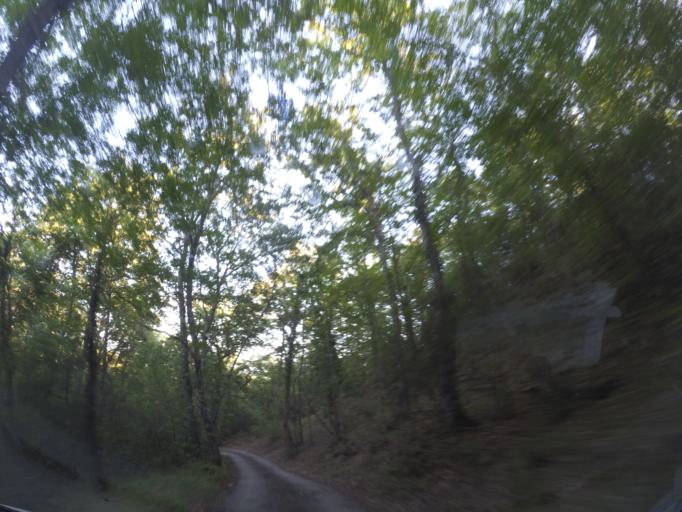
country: IT
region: Tuscany
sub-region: Province of Arezzo
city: Castiglion Fibocchi
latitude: 43.5565
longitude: 11.7872
